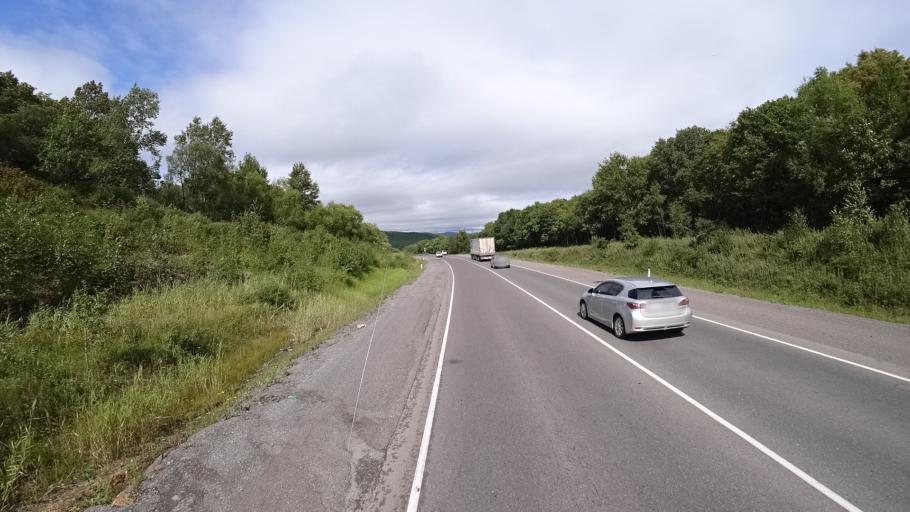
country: RU
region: Primorskiy
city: Lyalichi
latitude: 44.1305
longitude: 132.4270
